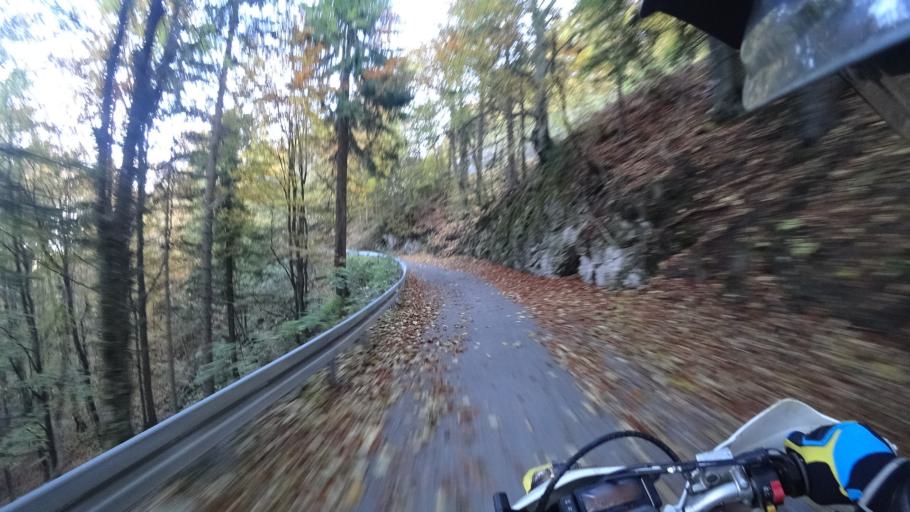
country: HR
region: Karlovacka
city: Plaski
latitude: 44.9941
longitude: 15.4129
